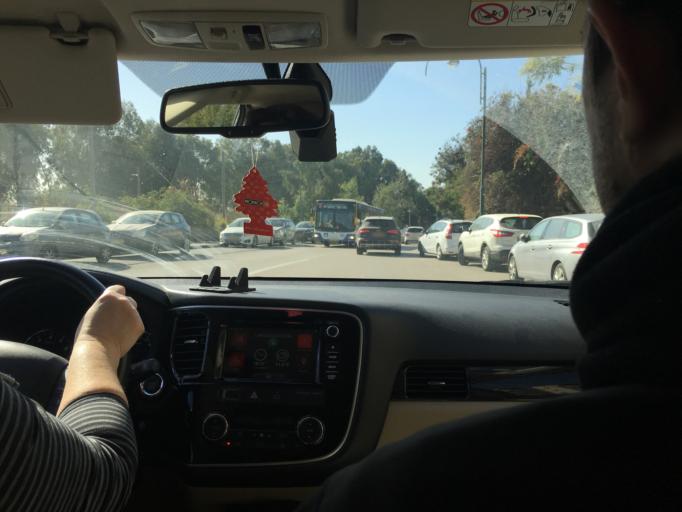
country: IL
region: Tel Aviv
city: Ramat HaSharon
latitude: 32.1408
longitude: 34.8462
